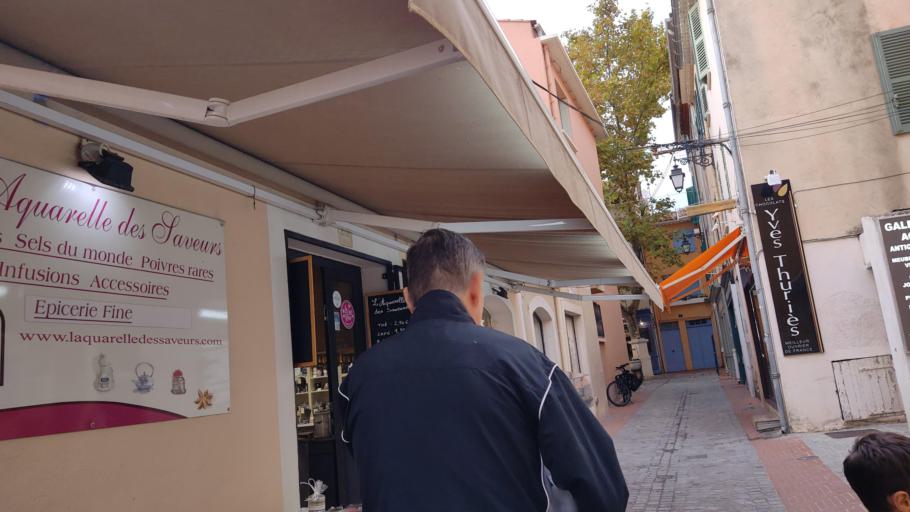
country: FR
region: Provence-Alpes-Cote d'Azur
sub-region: Departement du Var
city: Sanary-sur-Mer
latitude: 43.1187
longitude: 5.8025
